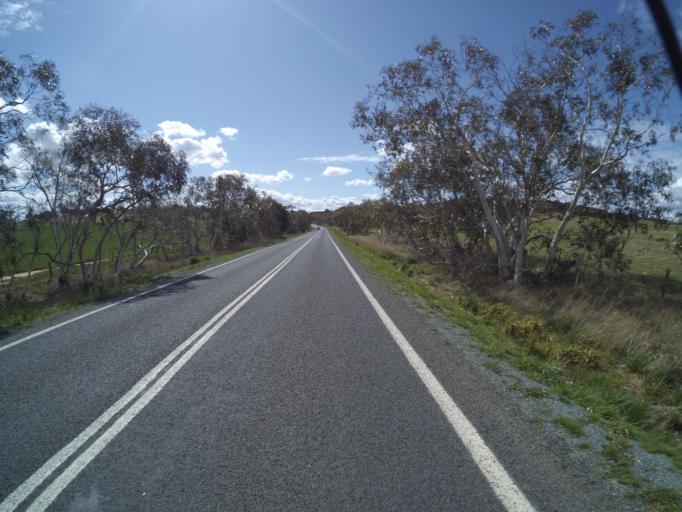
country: AU
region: New South Wales
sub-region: Goulburn Mulwaree
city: Goulburn
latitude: -34.8321
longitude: 149.6833
